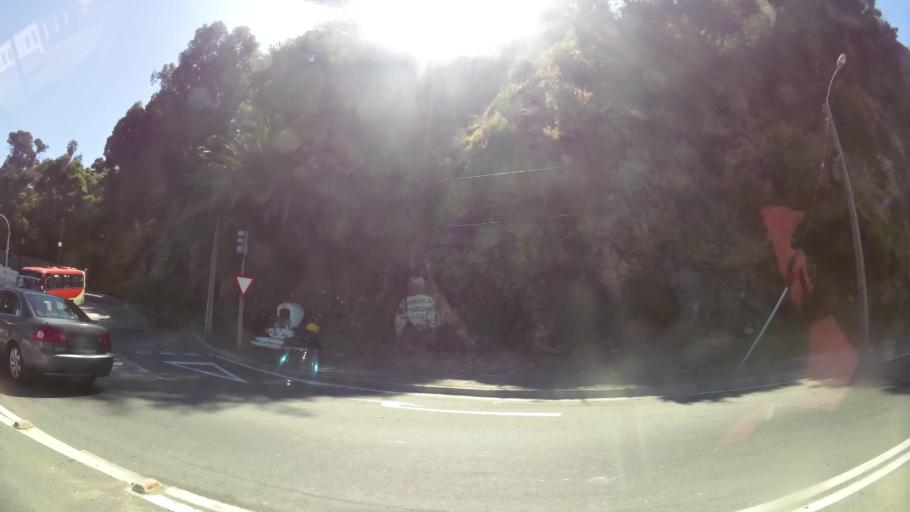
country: CL
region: Valparaiso
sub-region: Provincia de Valparaiso
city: Valparaiso
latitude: -33.0214
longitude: -71.6335
